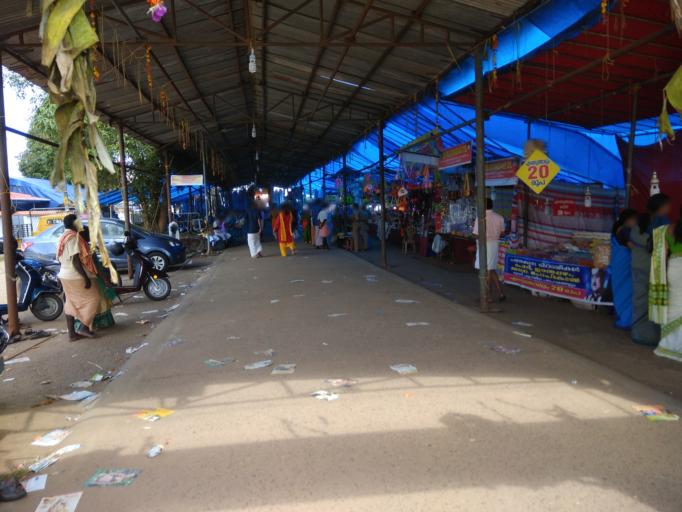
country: IN
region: Kerala
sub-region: Thrissur District
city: Irinjalakuda
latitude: 10.3467
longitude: 76.2027
